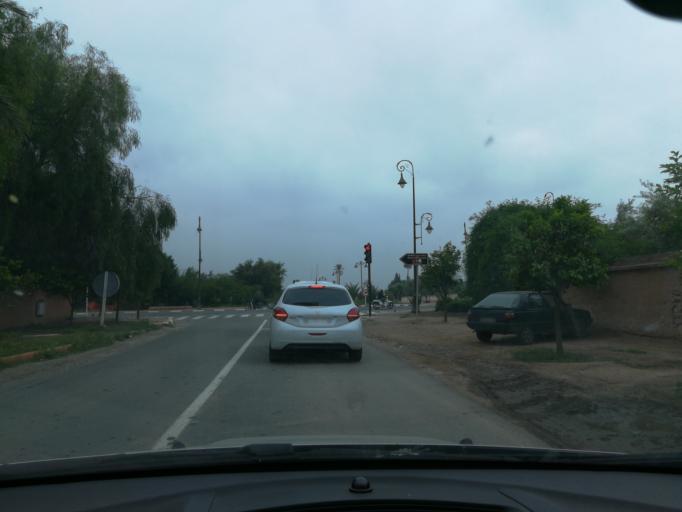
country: MA
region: Marrakech-Tensift-Al Haouz
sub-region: Marrakech
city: Marrakesh
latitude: 31.6471
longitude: -7.9730
